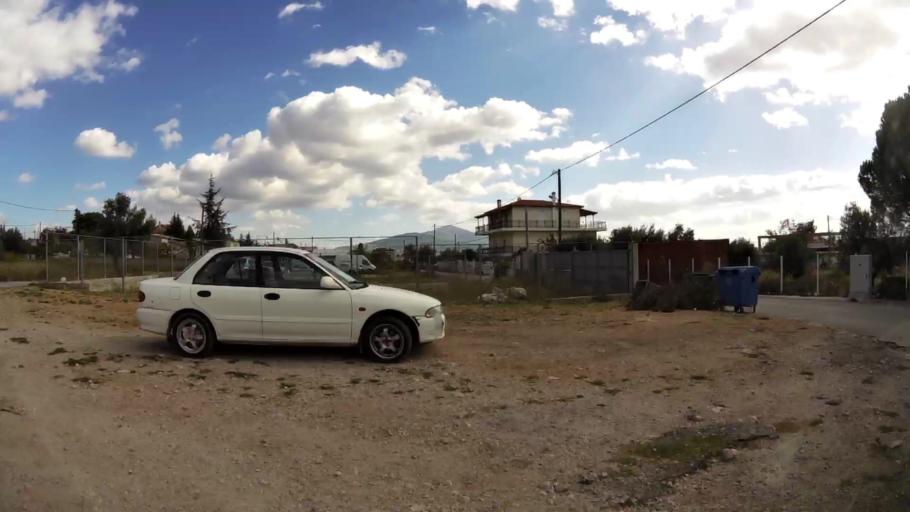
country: GR
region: Attica
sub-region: Nomarchia Anatolikis Attikis
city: Thrakomakedones
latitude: 38.1067
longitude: 23.7497
